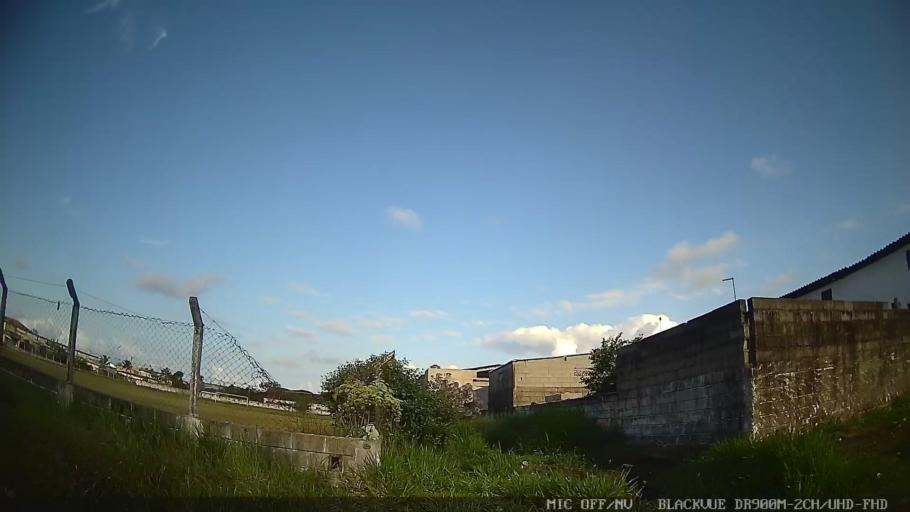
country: BR
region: Sao Paulo
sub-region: Itanhaem
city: Itanhaem
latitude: -24.1819
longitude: -46.8315
